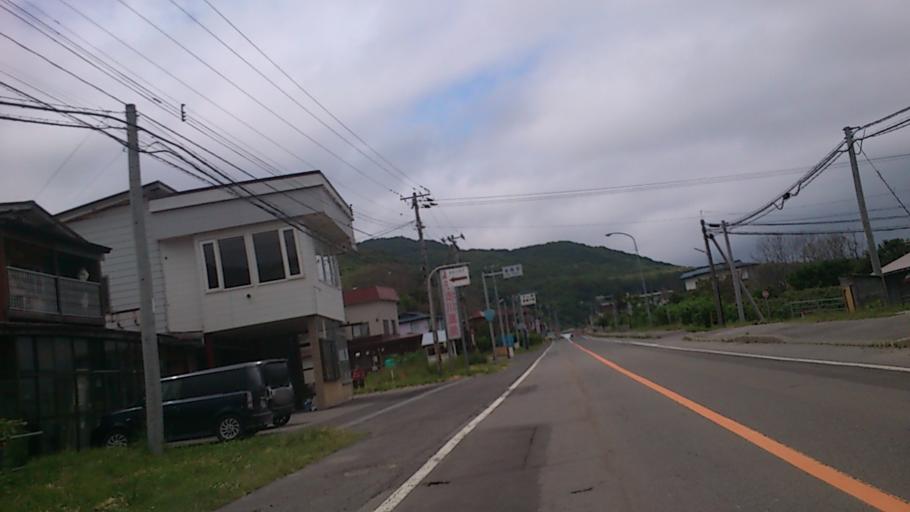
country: JP
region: Hokkaido
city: Iwanai
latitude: 42.6852
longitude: 140.0115
